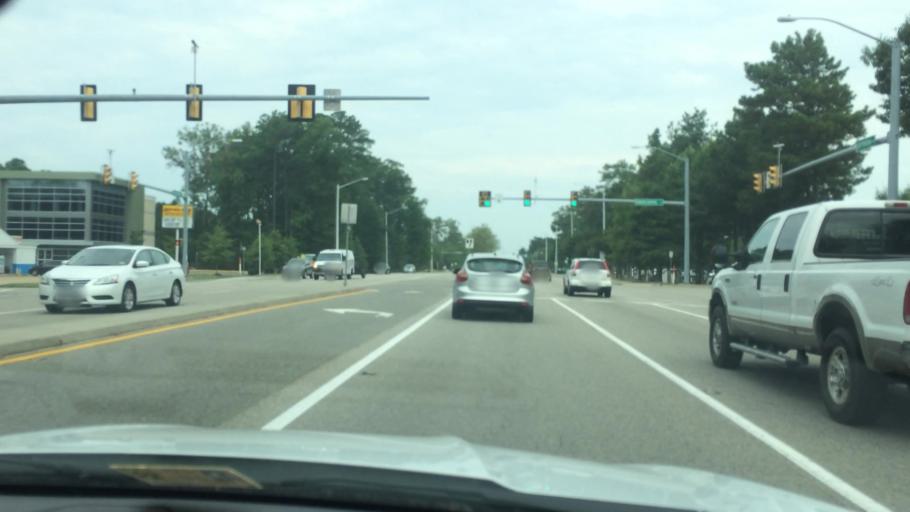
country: US
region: Virginia
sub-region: York County
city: Yorktown
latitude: 37.1552
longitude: -76.5330
